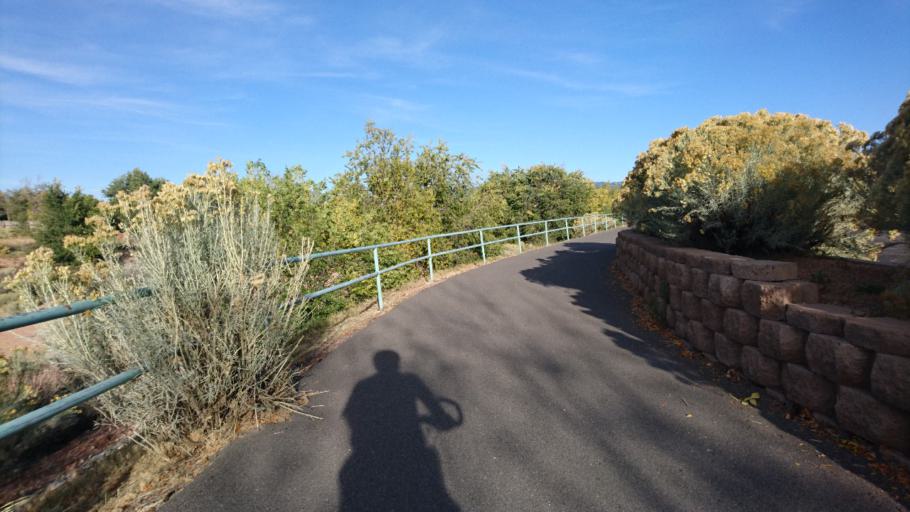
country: US
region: New Mexico
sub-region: Santa Fe County
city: Agua Fria
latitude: 35.6416
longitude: -106.0064
